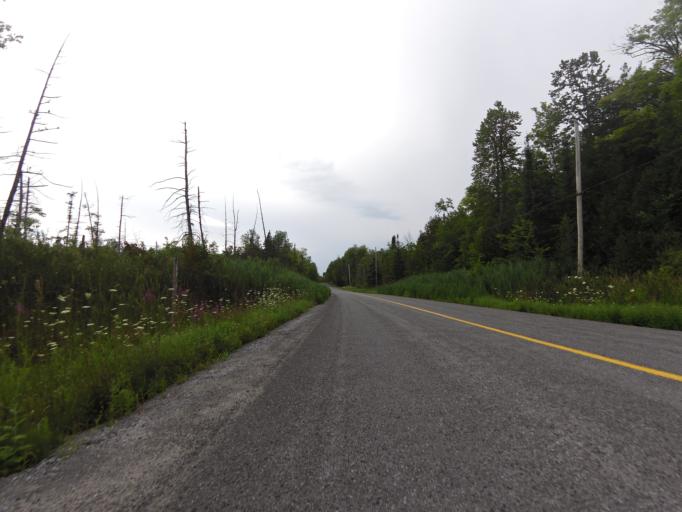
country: CA
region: Ontario
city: Perth
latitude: 44.8679
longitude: -76.5474
